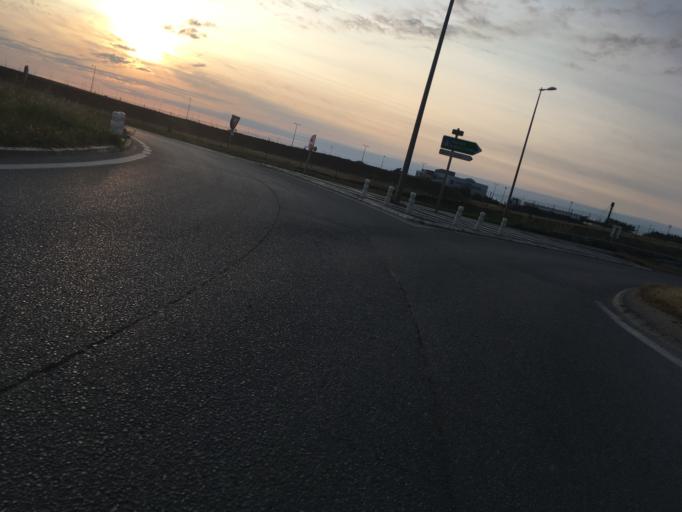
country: FR
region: Poitou-Charentes
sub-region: Departement de la Charente-Maritime
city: Rivedoux-Plage
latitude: 46.1729
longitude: -1.2174
